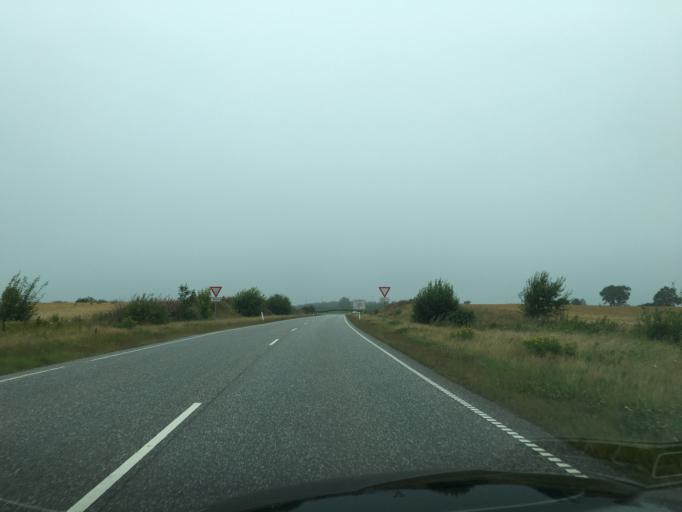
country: DK
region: South Denmark
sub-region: Kolding Kommune
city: Kolding
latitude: 55.5479
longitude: 9.4488
